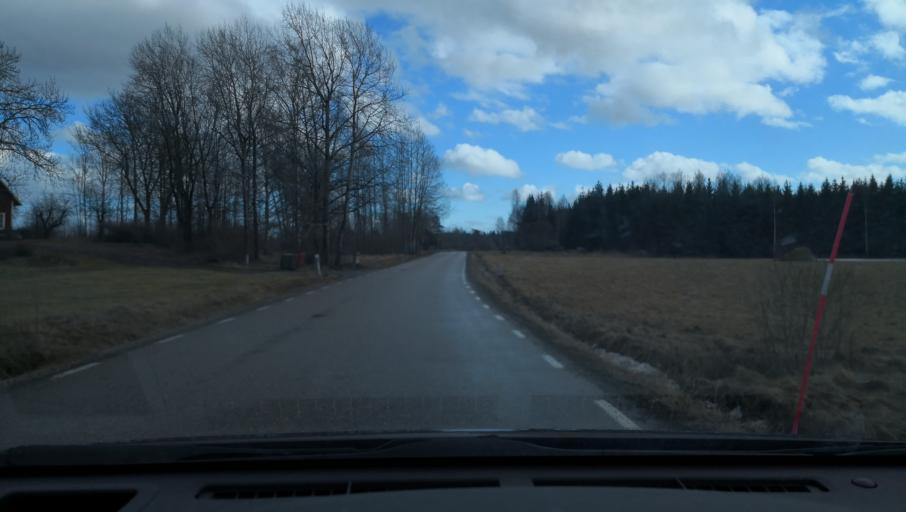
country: SE
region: OErebro
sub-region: Lindesbergs Kommun
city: Fellingsbro
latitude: 59.3519
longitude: 15.6759
